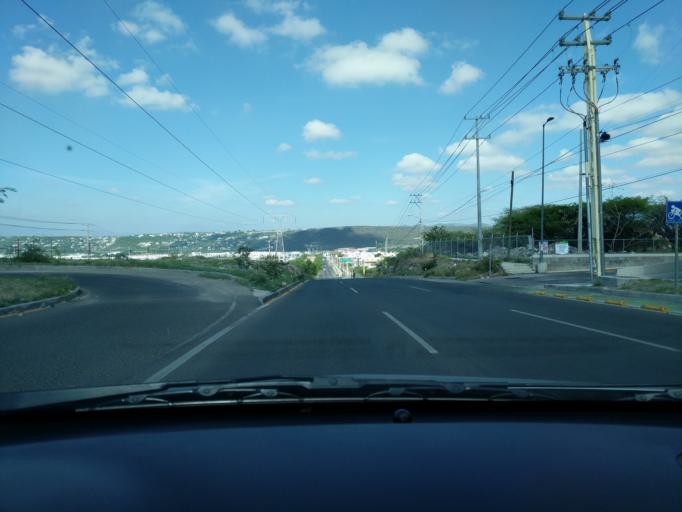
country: MX
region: Queretaro
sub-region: Queretaro
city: Patria Nueva
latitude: 20.6469
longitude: -100.4800
